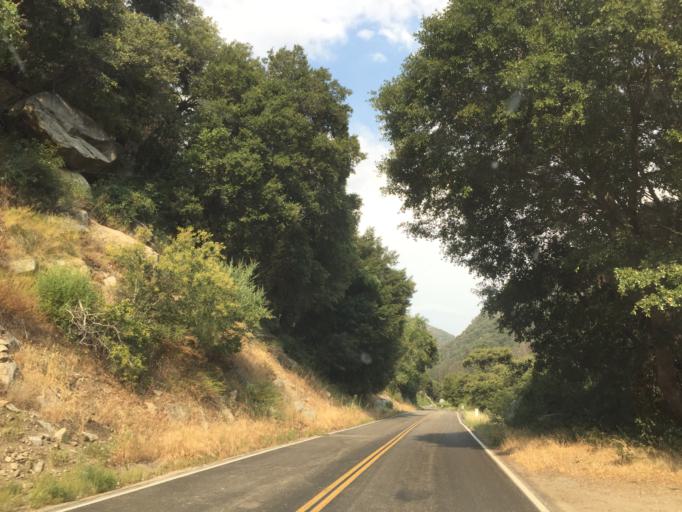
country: US
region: California
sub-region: Tulare County
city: Three Rivers
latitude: 36.8088
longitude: -118.7742
